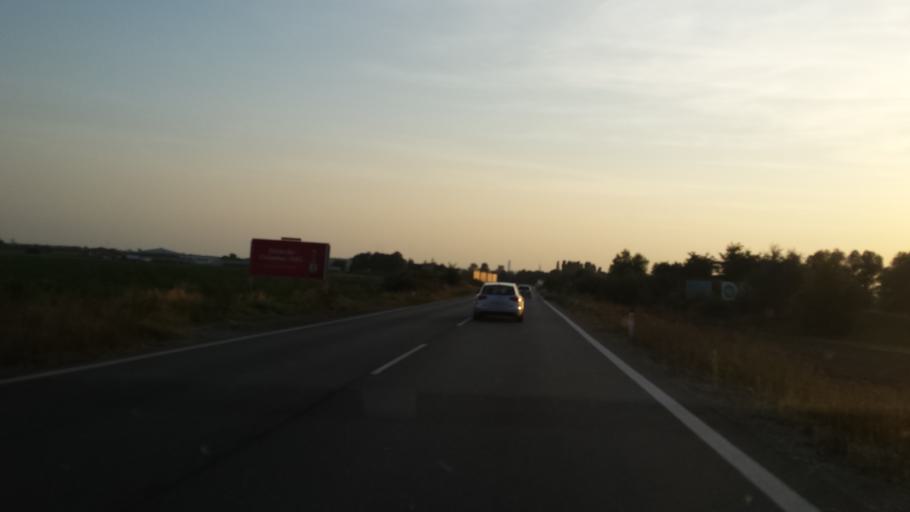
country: AT
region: Lower Austria
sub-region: Politischer Bezirk Ganserndorf
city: Aderklaa
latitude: 48.2802
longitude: 16.5069
